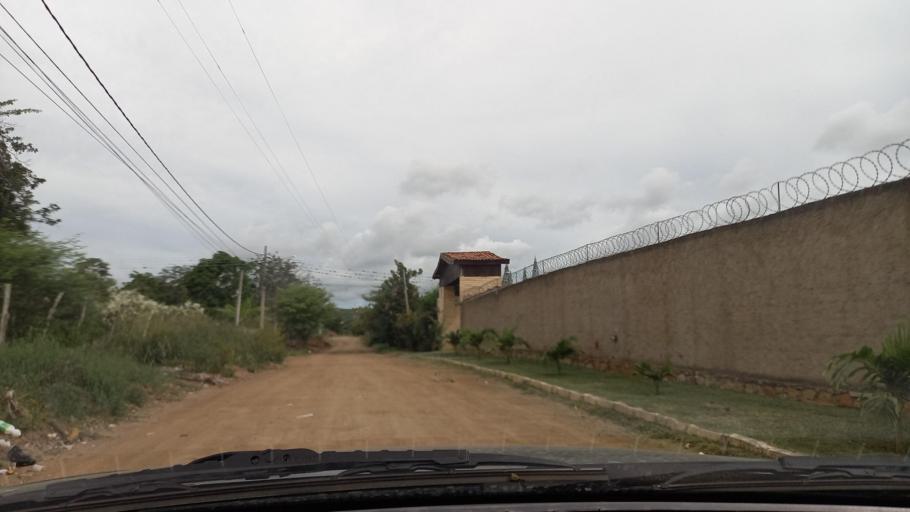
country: BR
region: Pernambuco
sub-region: Gravata
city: Gravata
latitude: -8.2013
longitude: -35.6007
